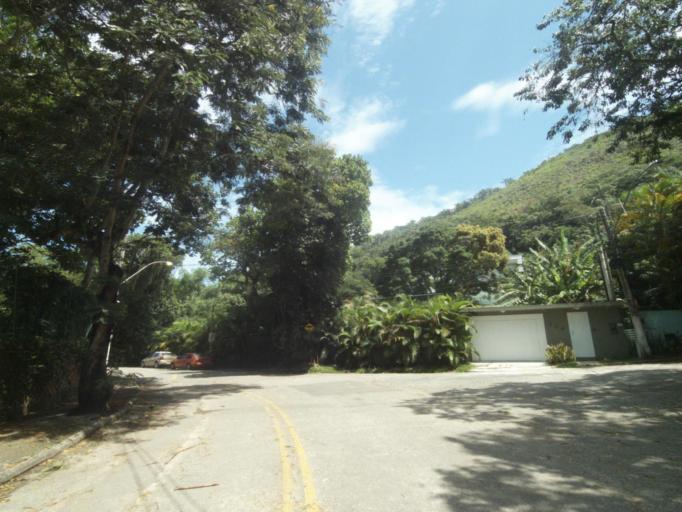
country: BR
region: Rio de Janeiro
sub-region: Niteroi
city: Niteroi
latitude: -22.9716
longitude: -43.0353
